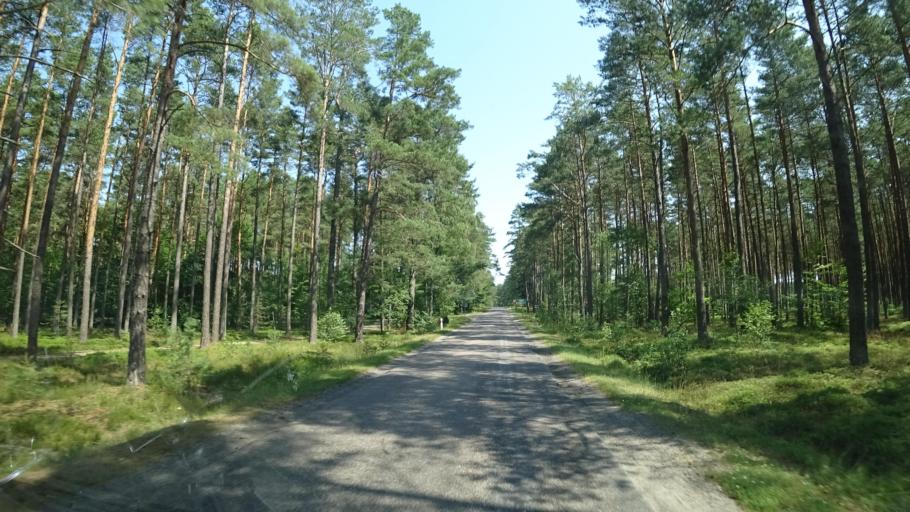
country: PL
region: Pomeranian Voivodeship
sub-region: Powiat chojnicki
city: Brusy
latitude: 53.8663
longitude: 17.6134
